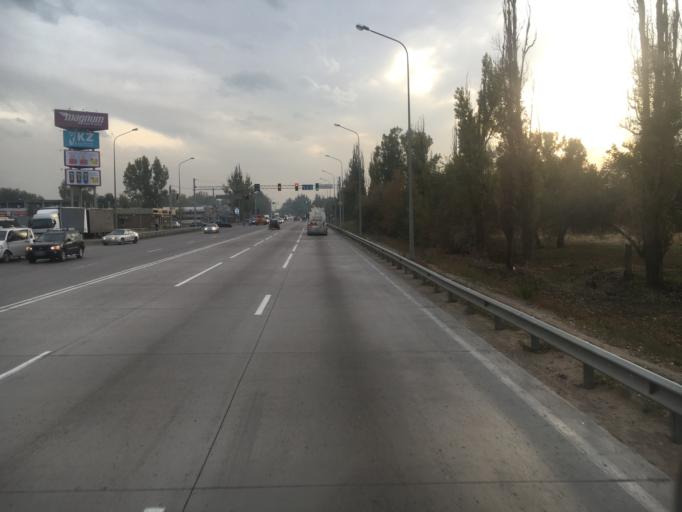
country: KZ
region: Almaty Oblysy
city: Pervomayskiy
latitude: 43.3693
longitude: 76.9488
